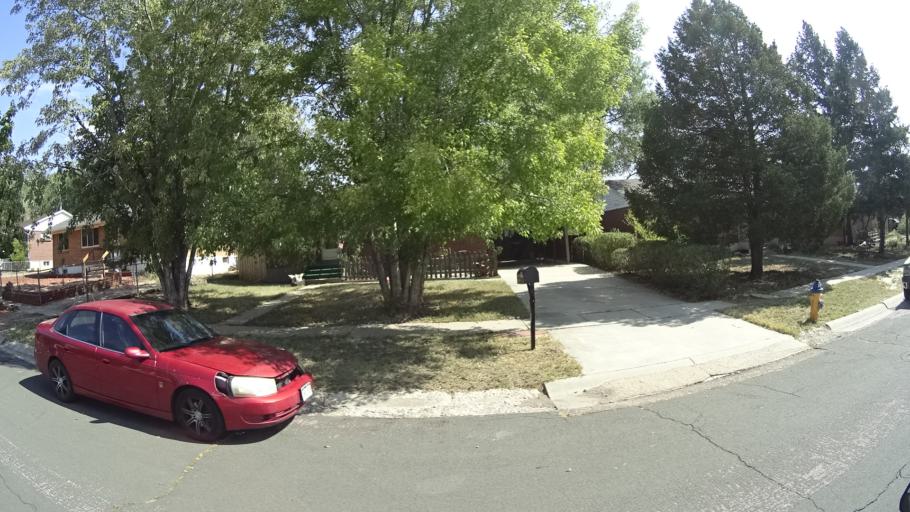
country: US
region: Colorado
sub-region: El Paso County
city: Colorado Springs
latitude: 38.8241
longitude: -104.7868
